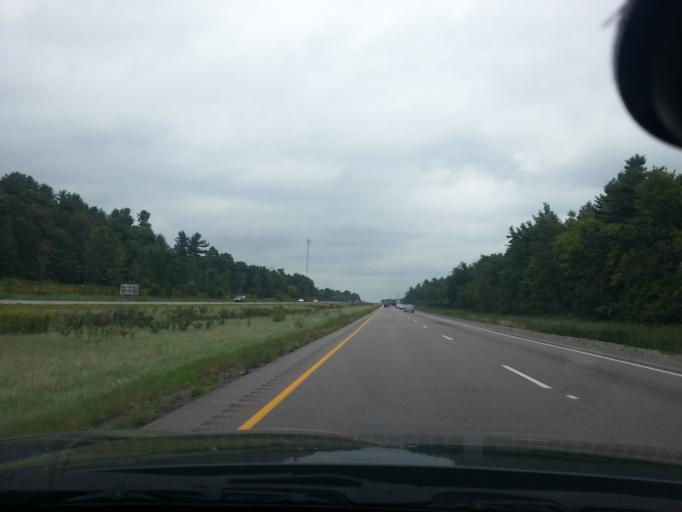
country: US
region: New York
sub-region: Jefferson County
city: Alexandria Bay
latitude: 44.4971
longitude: -75.8463
